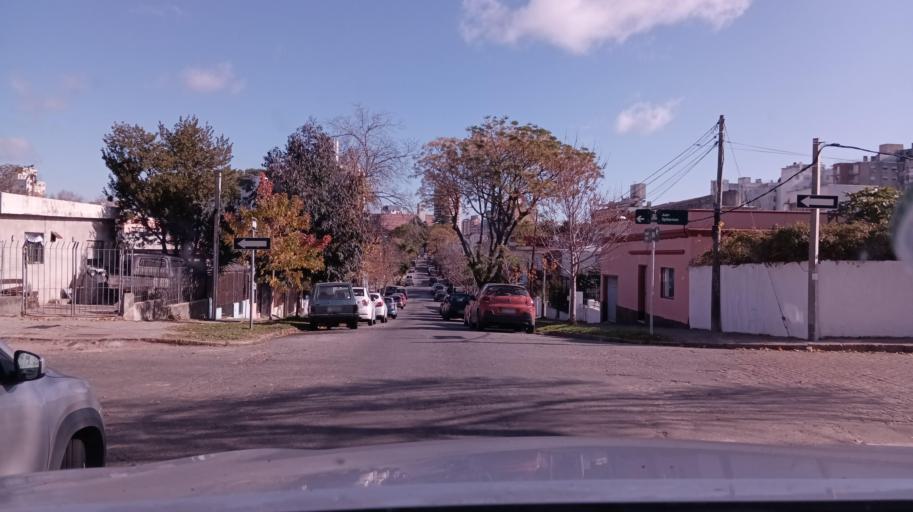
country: UY
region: Montevideo
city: Montevideo
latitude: -34.8878
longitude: -56.1503
